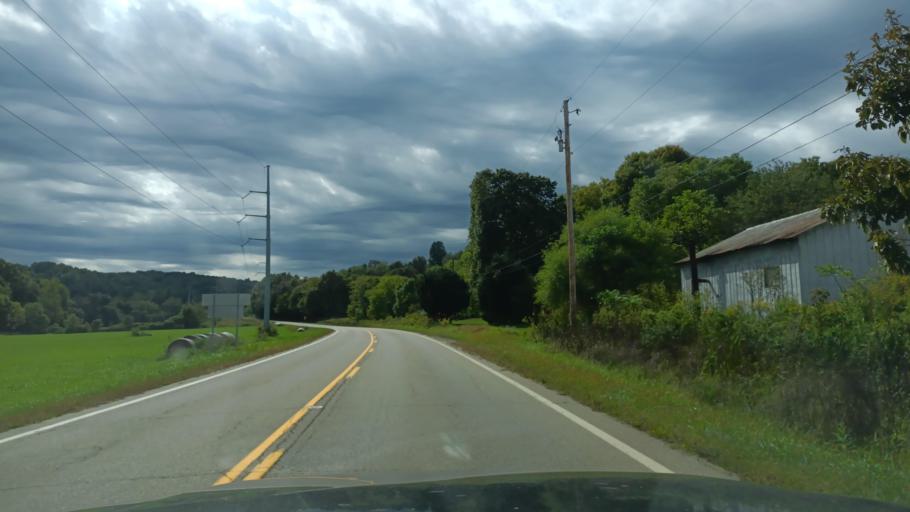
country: US
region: Ohio
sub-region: Vinton County
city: McArthur
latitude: 39.2402
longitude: -82.3685
